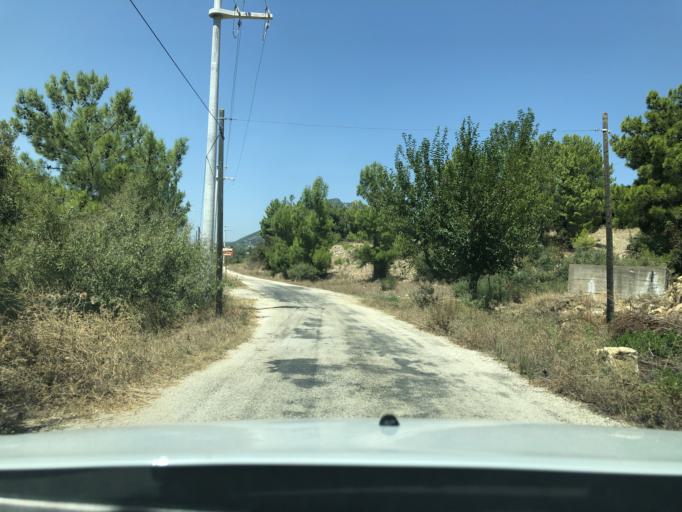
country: TR
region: Antalya
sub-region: Manavgat
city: Manavgat
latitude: 36.8726
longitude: 31.5513
